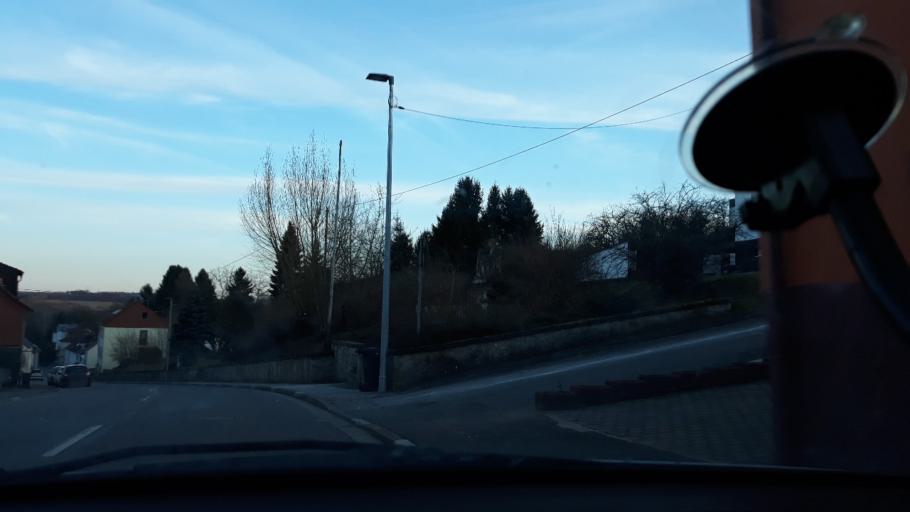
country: DE
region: Saarland
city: Sankt Ingbert
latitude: 49.2281
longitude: 7.1386
